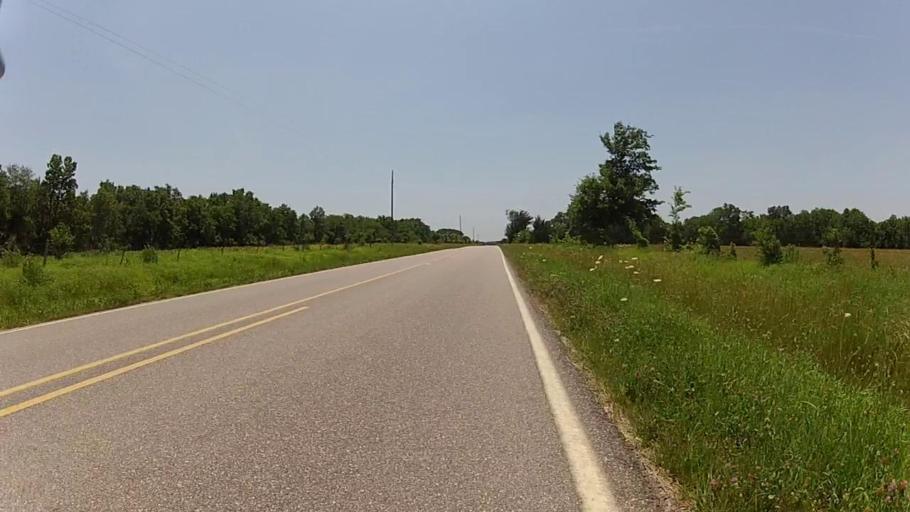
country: US
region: Kansas
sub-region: Montgomery County
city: Cherryvale
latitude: 37.2371
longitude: -95.5374
